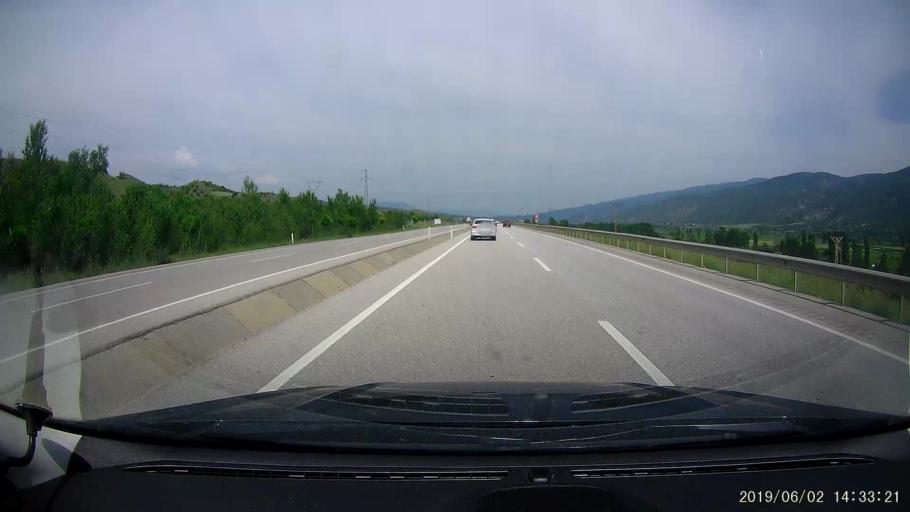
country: TR
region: Kastamonu
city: Tosya
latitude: 41.0310
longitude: 34.1689
